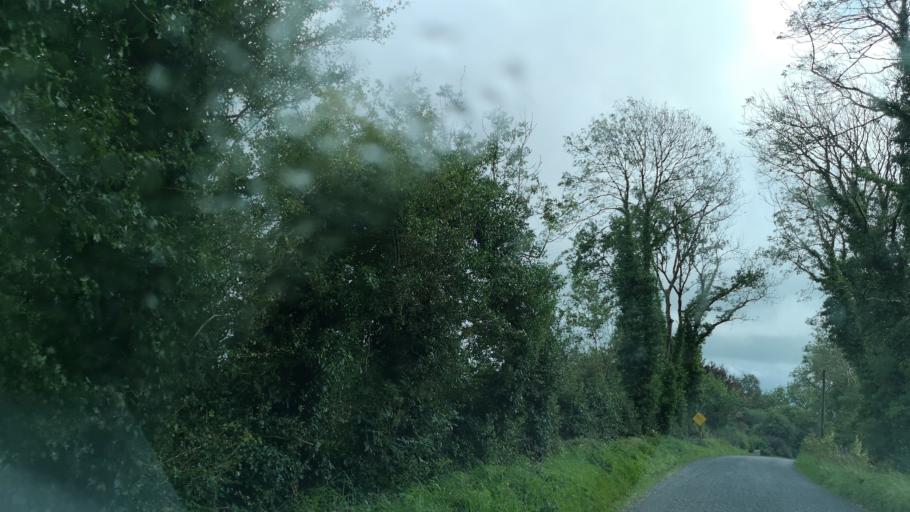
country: IE
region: Connaught
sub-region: County Galway
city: Loughrea
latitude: 53.3047
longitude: -8.6149
